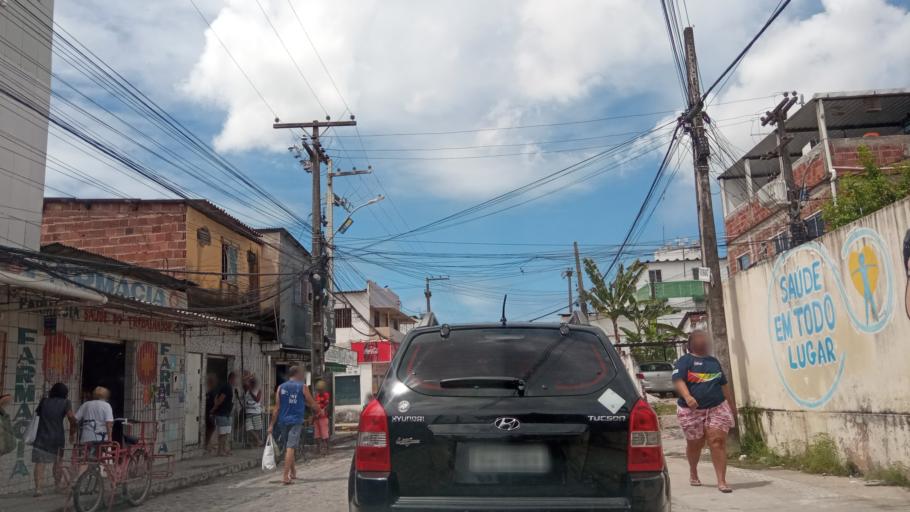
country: BR
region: Pernambuco
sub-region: Jaboatao Dos Guararapes
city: Jaboatao dos Guararapes
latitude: -8.1150
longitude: -34.9369
